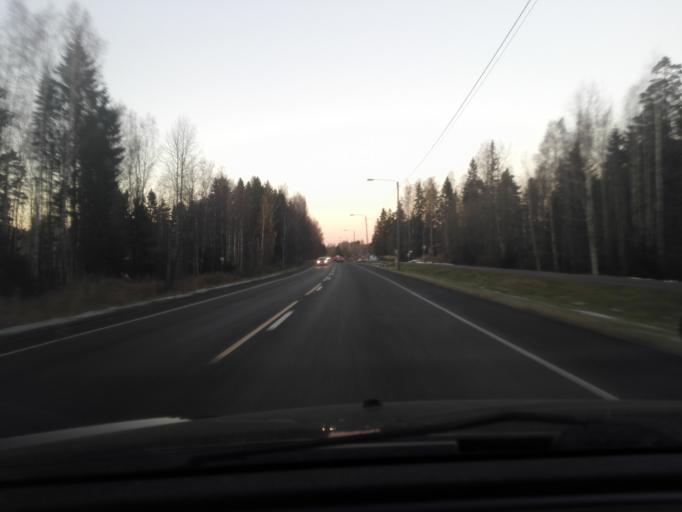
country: FI
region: Uusimaa
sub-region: Helsinki
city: Kerava
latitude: 60.3341
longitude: 25.1247
